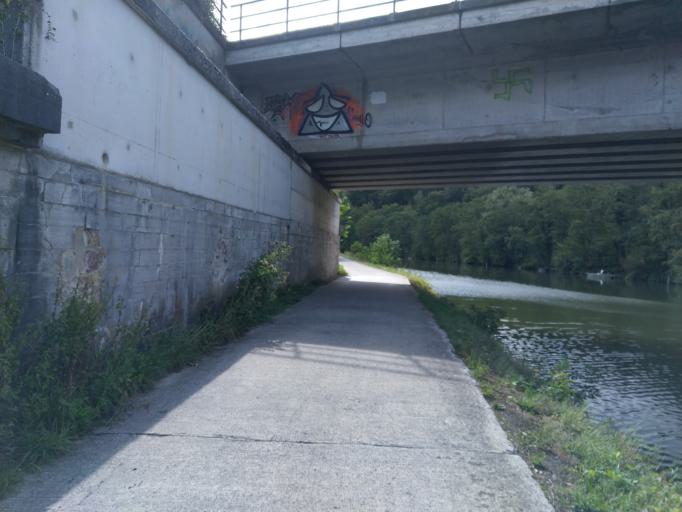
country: BE
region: Wallonia
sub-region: Province du Hainaut
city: Lobbes
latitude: 50.3469
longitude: 4.2564
